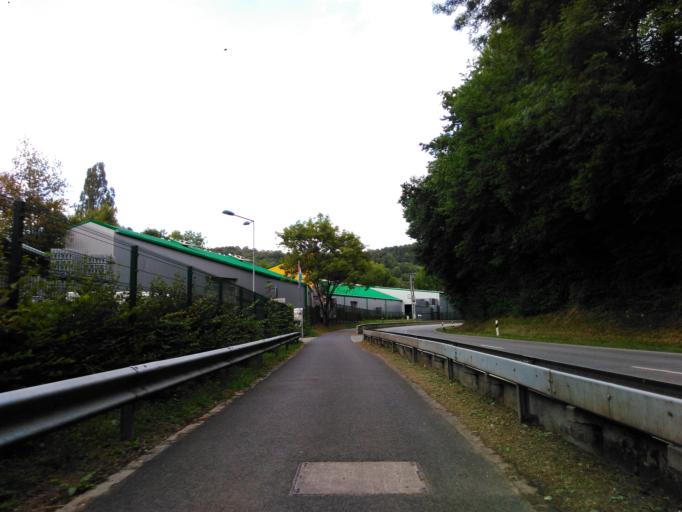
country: DE
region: Rheinland-Pfalz
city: Ralingen
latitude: 49.8113
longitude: 6.4940
